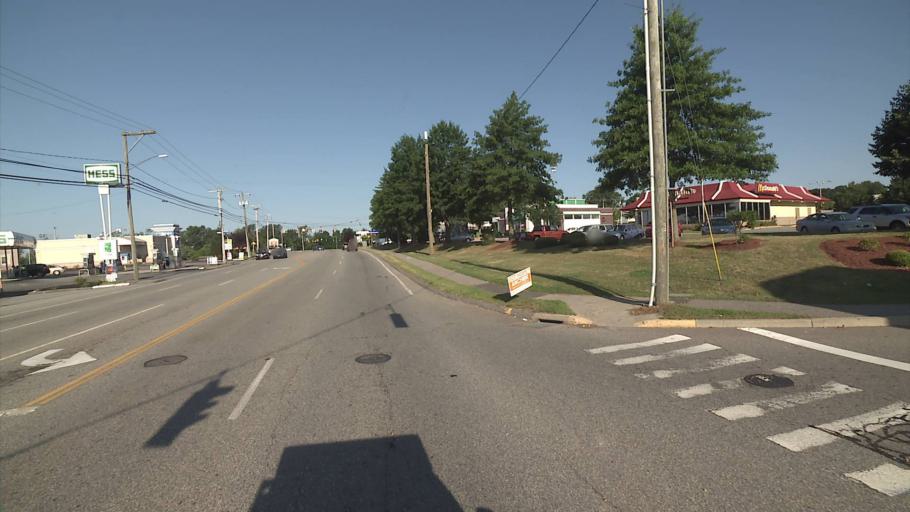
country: US
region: Connecticut
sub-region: New London County
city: Central Waterford
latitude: 41.3422
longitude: -72.1244
